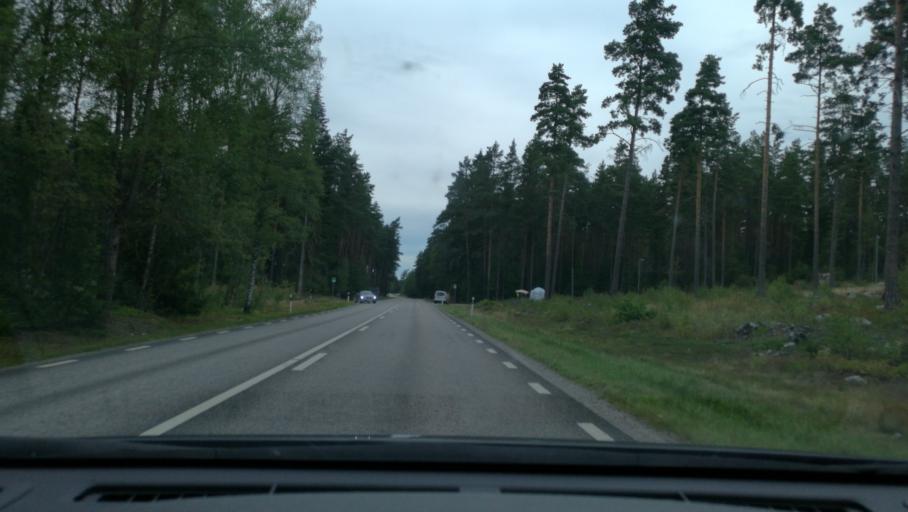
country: SE
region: Soedermanland
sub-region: Katrineholms Kommun
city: Katrineholm
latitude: 59.0967
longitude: 16.1909
